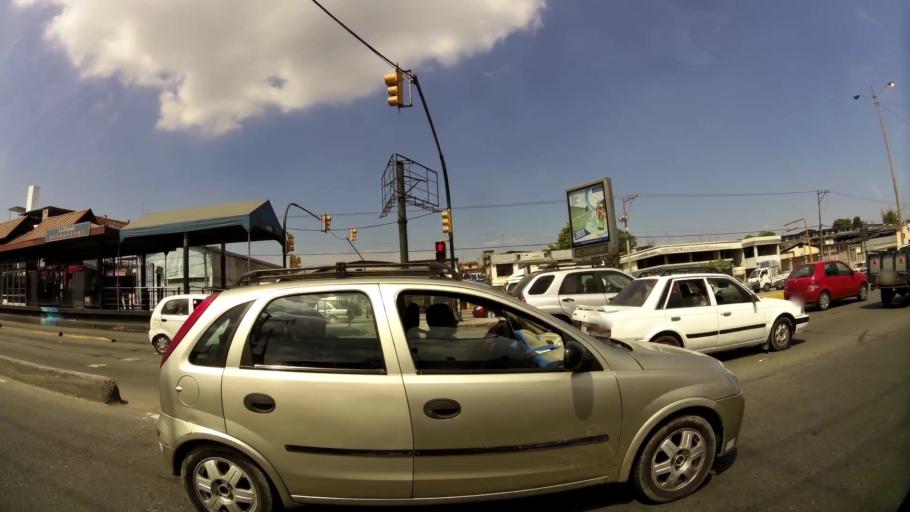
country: EC
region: Guayas
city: Guayaquil
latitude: -2.1266
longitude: -79.9319
